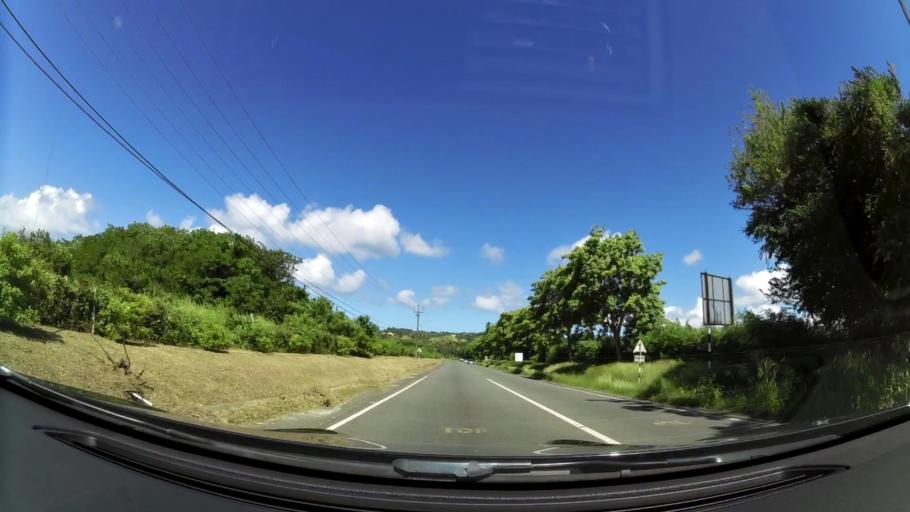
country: TT
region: Tobago
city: Scarborough
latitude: 11.1647
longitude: -60.7716
